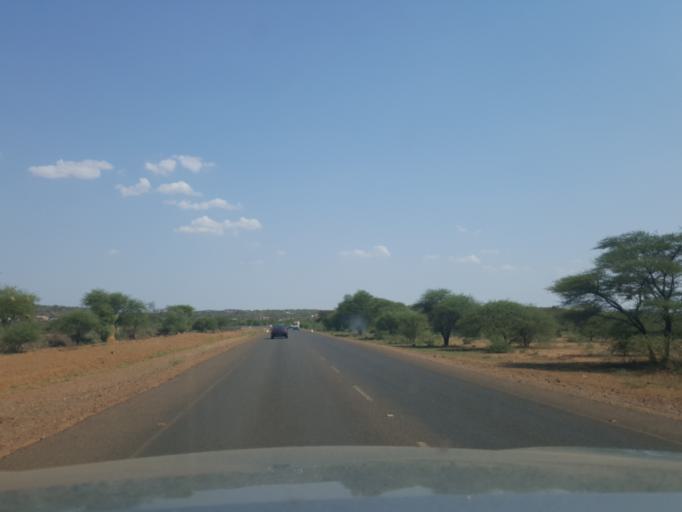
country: BW
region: South East
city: Ramotswa
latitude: -24.8554
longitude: 25.8293
